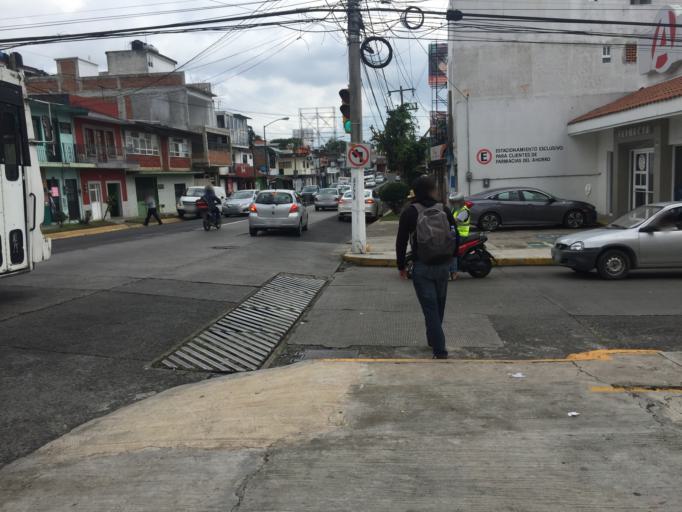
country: MX
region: Veracruz
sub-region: Xalapa
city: Xalapa de Enriquez
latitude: 19.5267
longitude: -96.9096
